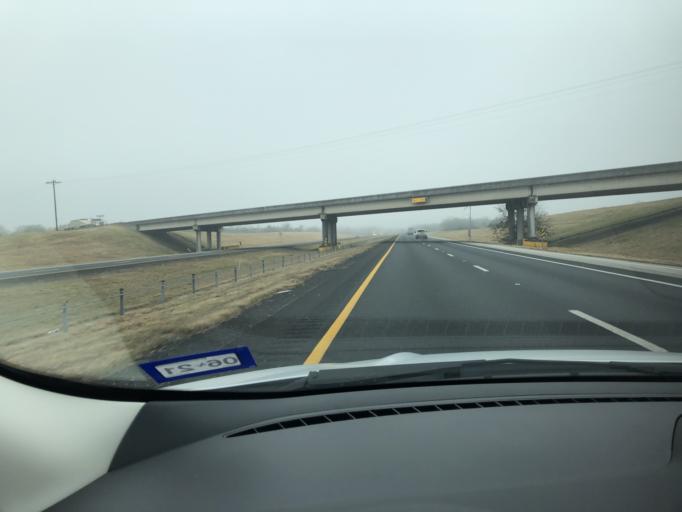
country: US
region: Texas
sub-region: Gonzales County
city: Waelder
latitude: 29.6695
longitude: -97.3002
